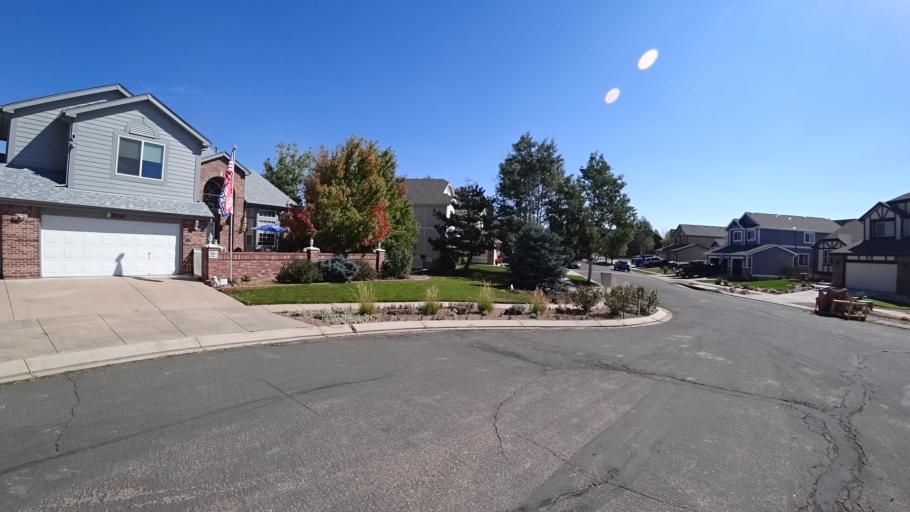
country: US
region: Colorado
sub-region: El Paso County
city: Cimarron Hills
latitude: 38.9013
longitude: -104.6955
